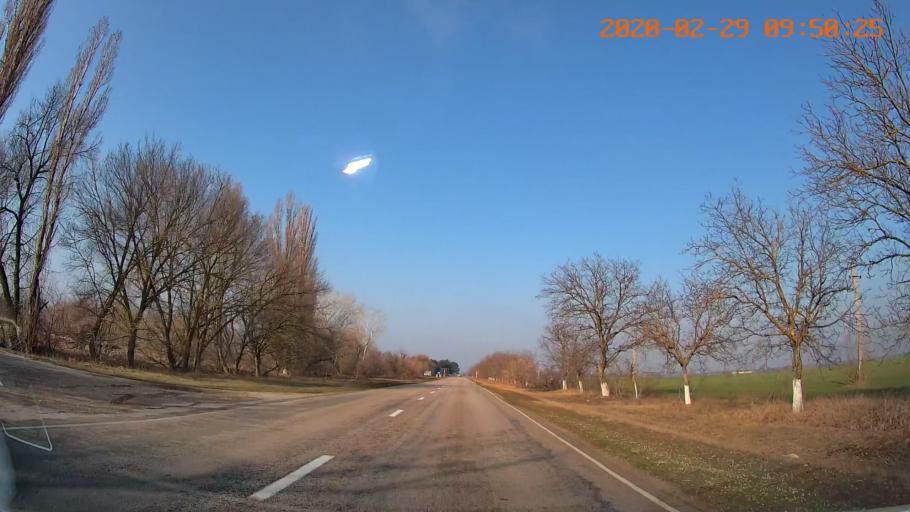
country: MD
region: Telenesti
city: Slobozia
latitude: 46.7022
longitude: 29.7559
